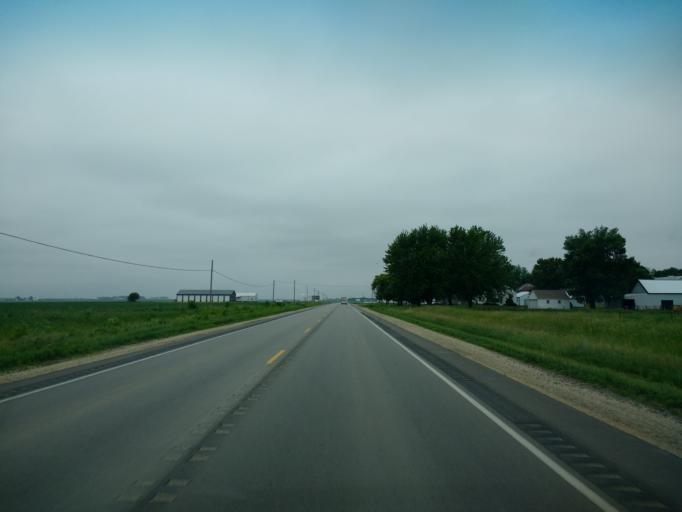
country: US
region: Iowa
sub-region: O'Brien County
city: Hartley
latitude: 43.1850
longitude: -95.4942
